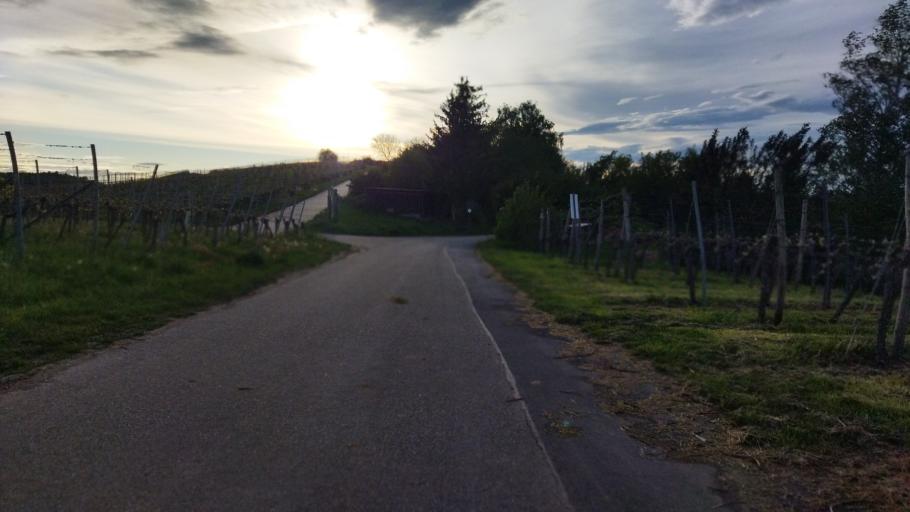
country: DE
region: Baden-Wuerttemberg
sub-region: Regierungsbezirk Stuttgart
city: Flein
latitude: 49.0961
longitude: 9.2288
